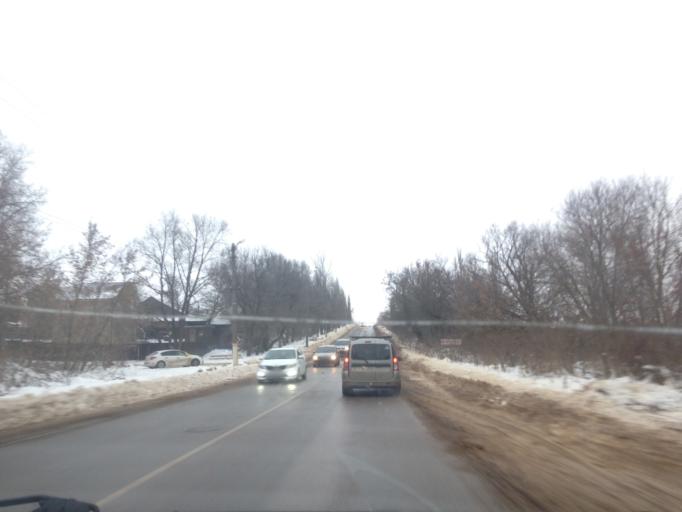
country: RU
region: Tula
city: Shchekino
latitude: 53.9946
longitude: 37.5077
